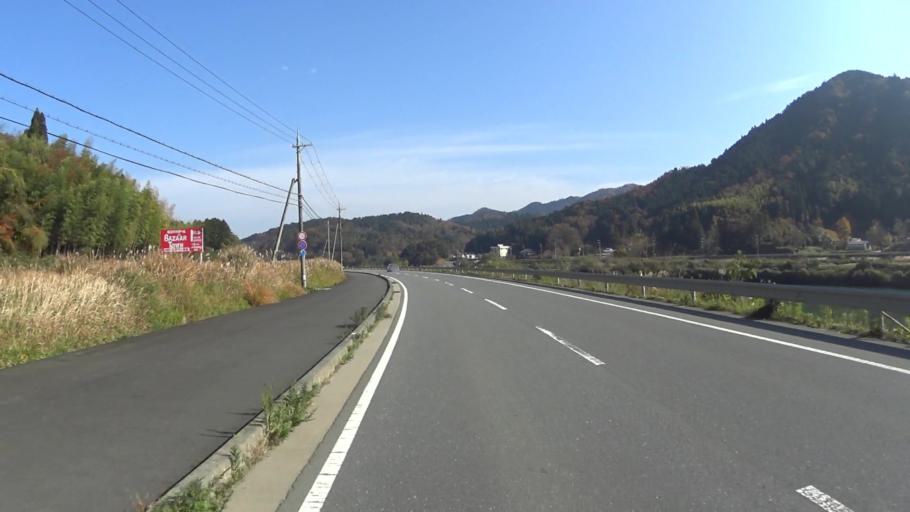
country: JP
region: Kyoto
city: Miyazu
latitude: 35.4114
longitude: 135.1972
